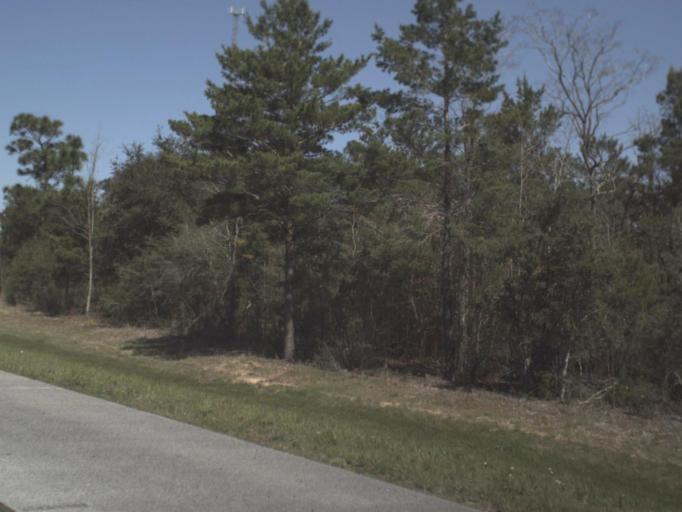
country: US
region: Florida
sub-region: Walton County
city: DeFuniak Springs
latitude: 30.7461
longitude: -86.2349
